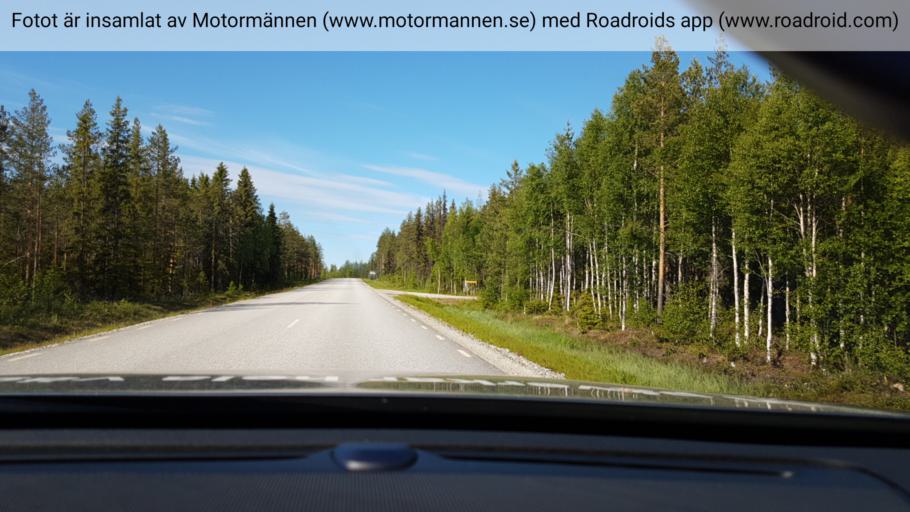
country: SE
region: Vaesterbotten
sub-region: Bjurholms Kommun
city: Bjurholm
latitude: 64.1565
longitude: 19.3602
